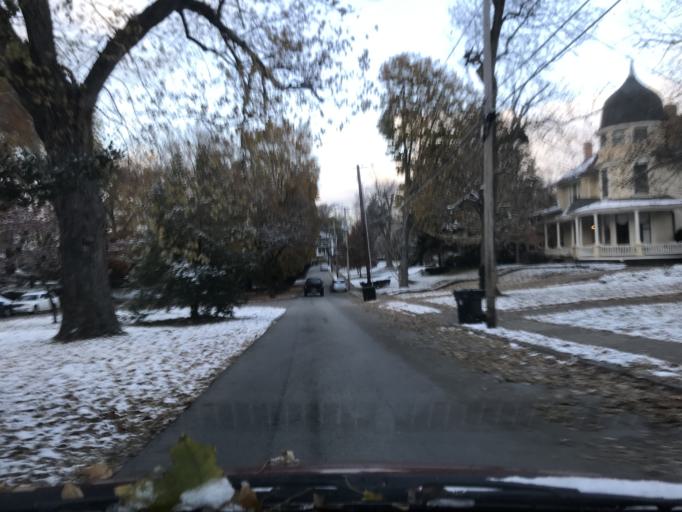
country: US
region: Kentucky
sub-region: Jefferson County
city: Indian Hills
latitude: 38.2555
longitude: -85.6946
